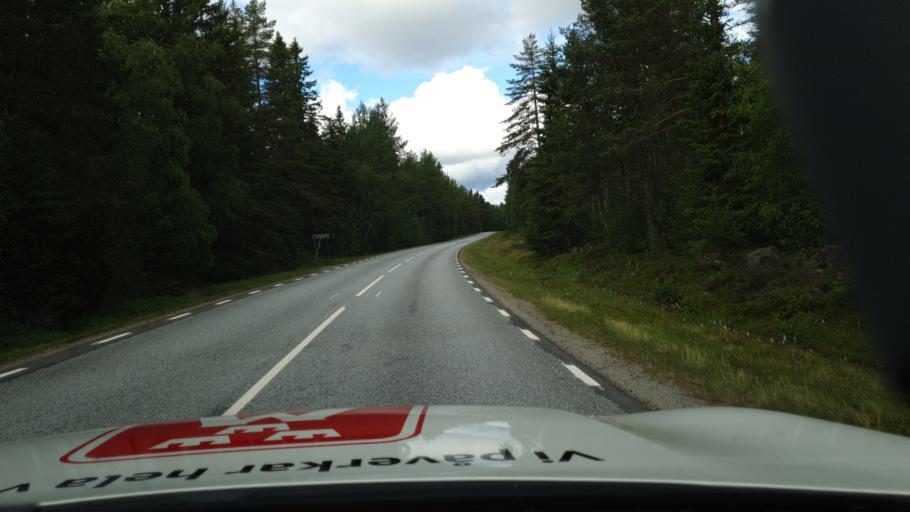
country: SE
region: Vaesterbotten
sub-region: Umea Kommun
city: Roback
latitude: 63.6713
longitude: 20.1742
